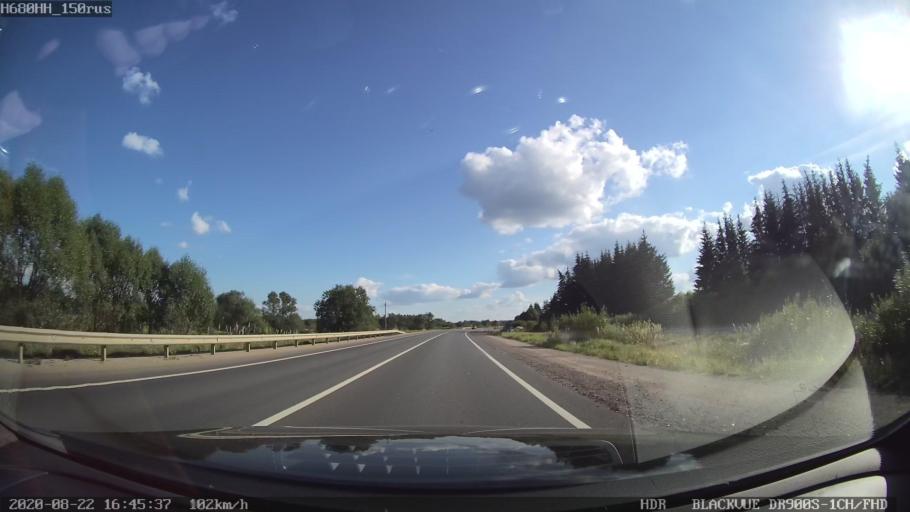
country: RU
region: Tverskaya
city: Rameshki
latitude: 57.2924
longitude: 36.0898
